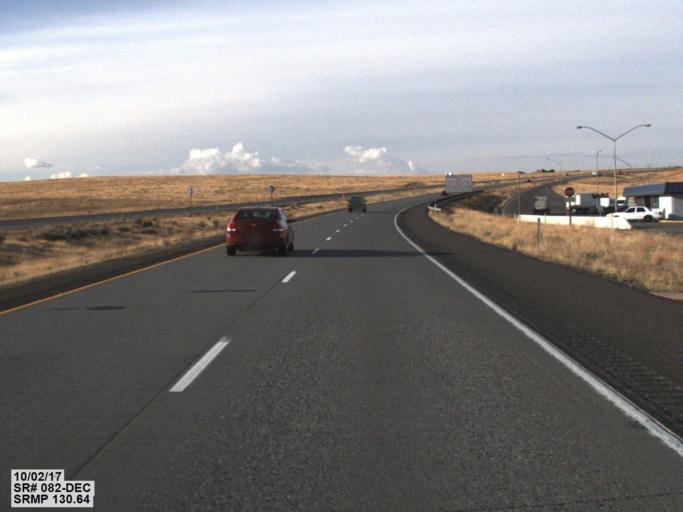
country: US
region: Oregon
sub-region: Umatilla County
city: Umatilla
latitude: 45.9585
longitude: -119.3413
